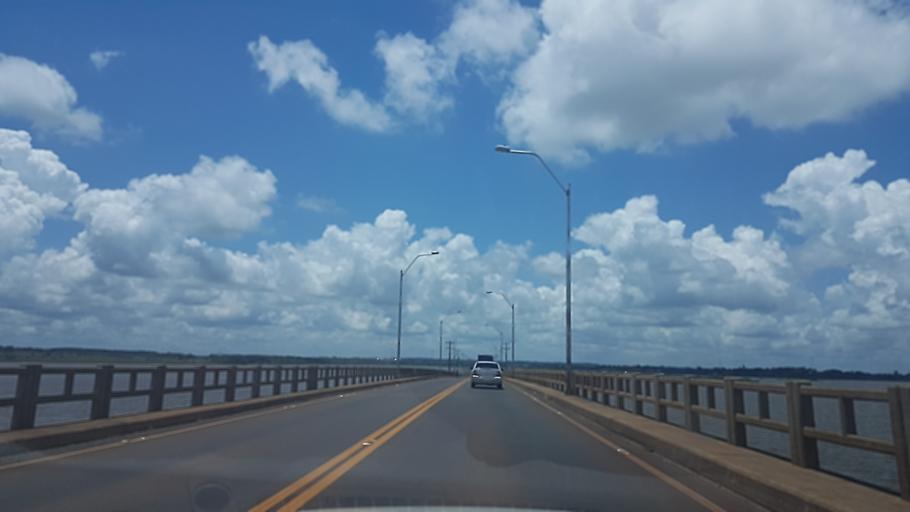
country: PY
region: Itapua
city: Carmen del Parana
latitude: -27.2050
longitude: -56.1694
